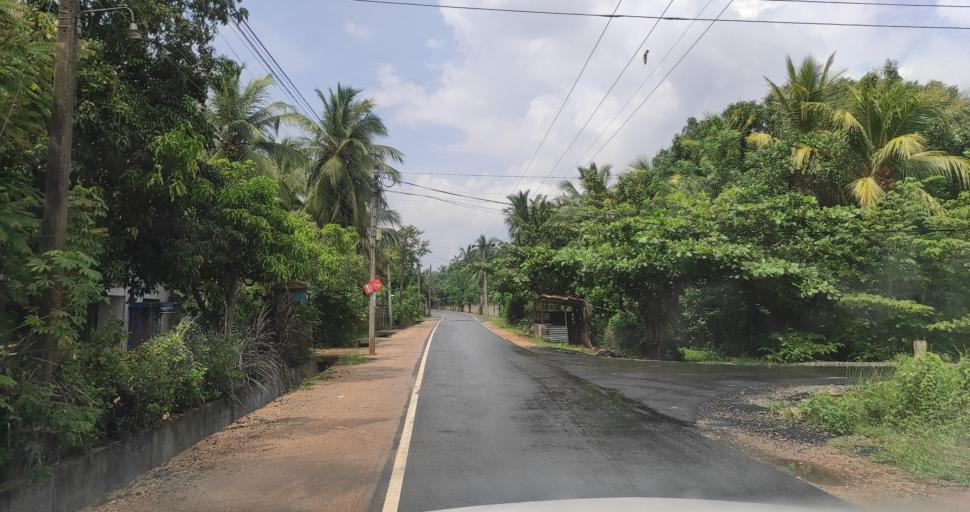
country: LK
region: Eastern Province
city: Trincomalee
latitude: 8.3744
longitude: 81.0089
